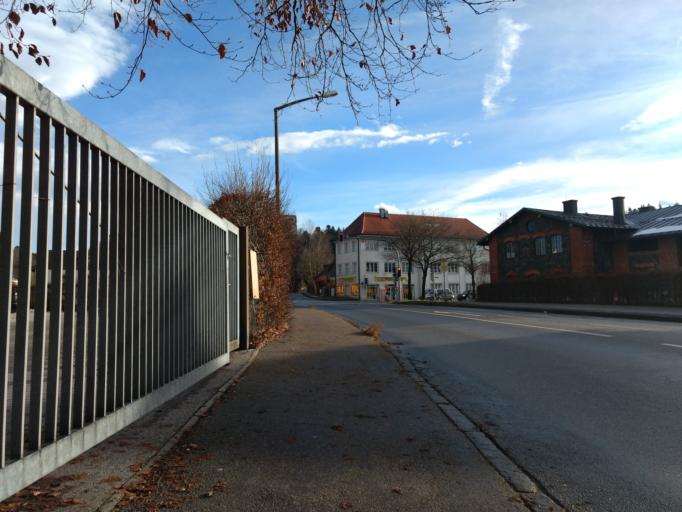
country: DE
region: Bavaria
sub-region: Upper Bavaria
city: Traunstein
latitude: 47.8665
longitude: 12.6474
